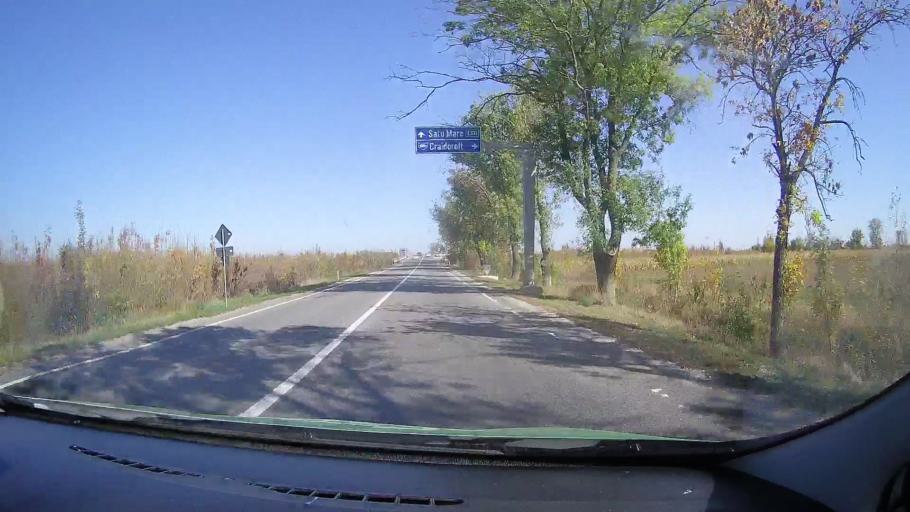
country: RO
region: Satu Mare
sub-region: Comuna Moftinu
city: Moftinu Mic
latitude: 47.7046
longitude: 22.6336
